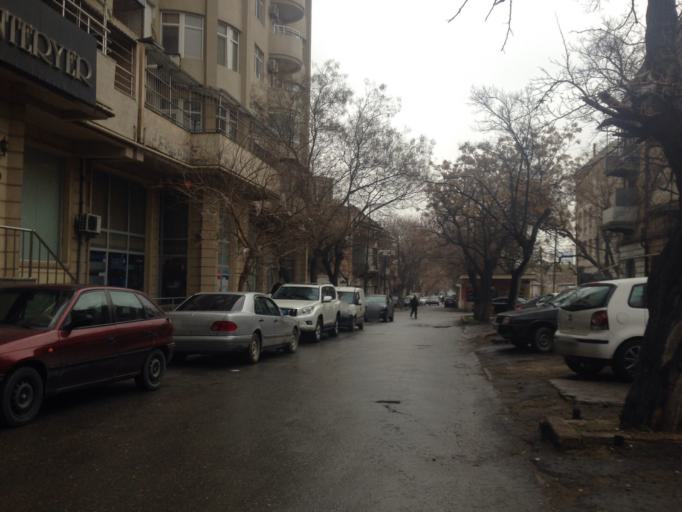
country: AZ
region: Baki
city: Baku
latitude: 40.3902
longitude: 49.8558
